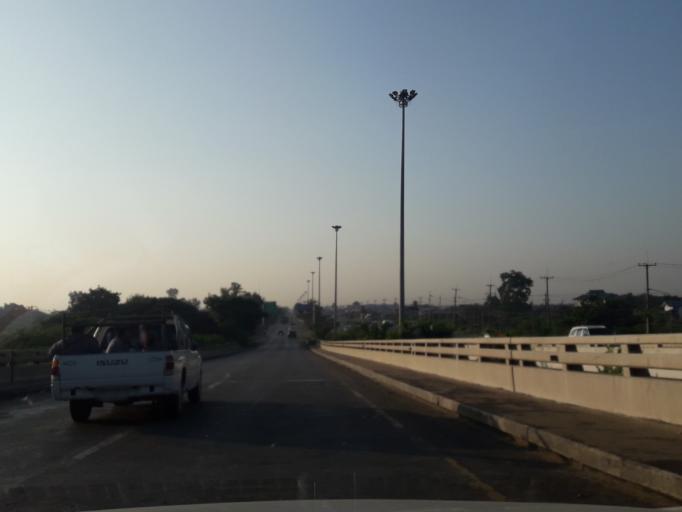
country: TH
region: Phra Nakhon Si Ayutthaya
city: Bang Pa-in
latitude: 14.1929
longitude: 100.5531
